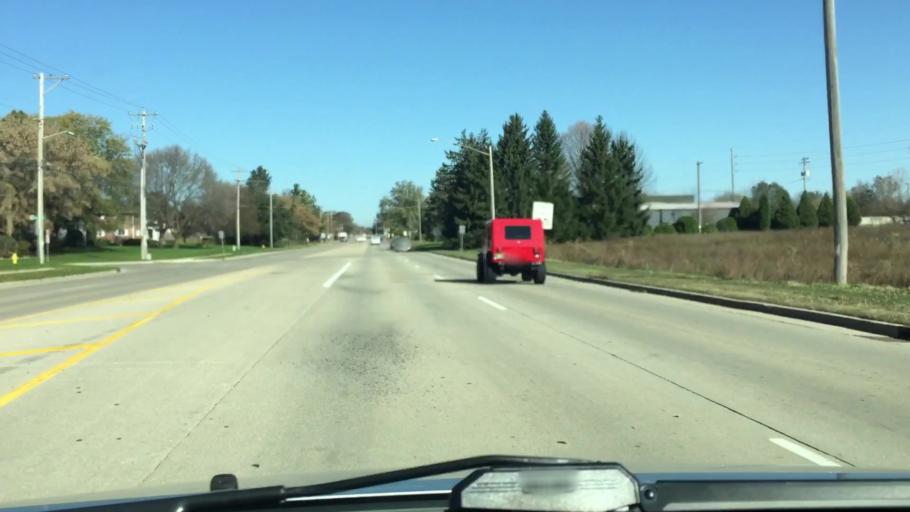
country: US
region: Wisconsin
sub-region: Waukesha County
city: Sussex
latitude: 43.1253
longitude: -88.2096
